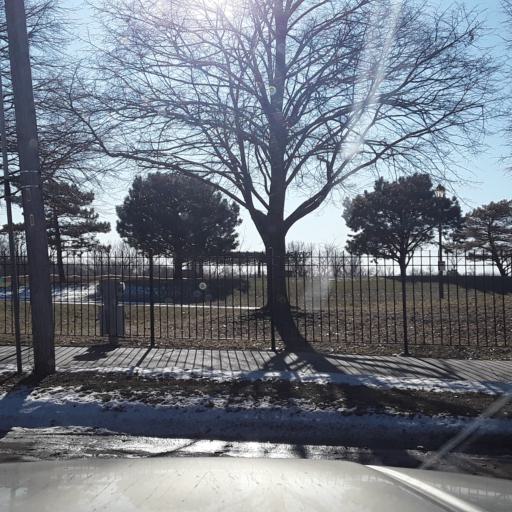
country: US
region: Nebraska
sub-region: Adams County
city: Hastings
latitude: 40.5785
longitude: -98.4096
